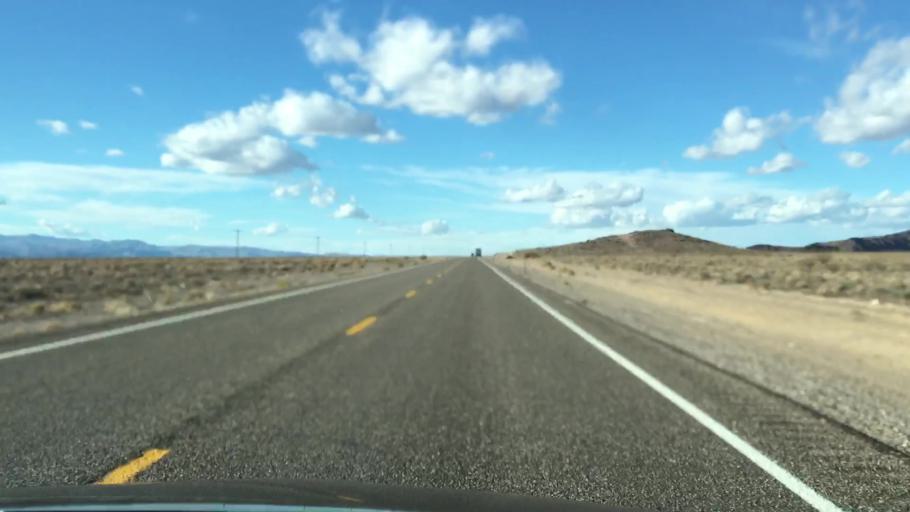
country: US
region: Nevada
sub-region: Nye County
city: Beatty
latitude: 37.1903
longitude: -116.9431
